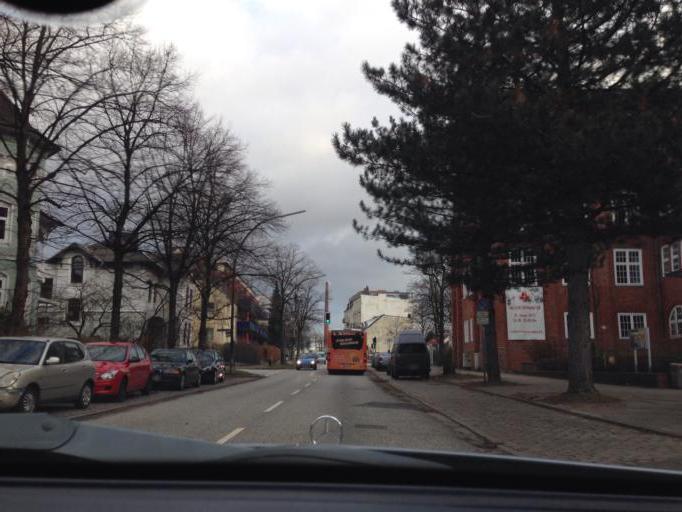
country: DE
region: Hamburg
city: Marienthal
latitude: 53.5728
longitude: 10.0780
